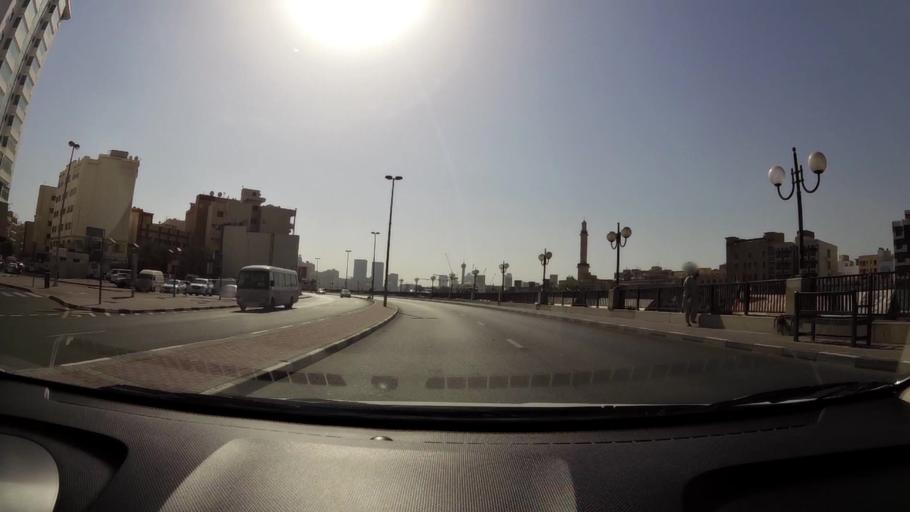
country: AE
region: Ash Shariqah
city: Sharjah
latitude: 25.2658
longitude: 55.2941
